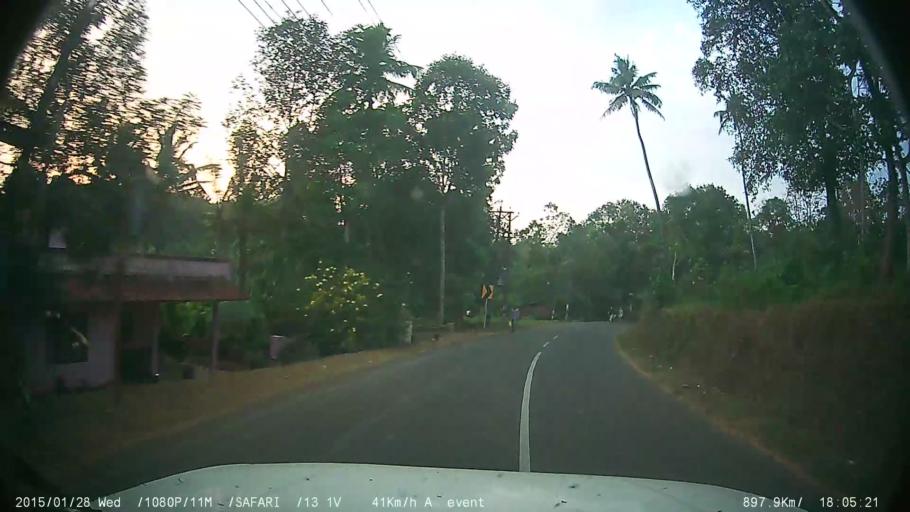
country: IN
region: Kerala
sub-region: Kottayam
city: Palackattumala
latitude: 9.7251
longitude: 76.5794
